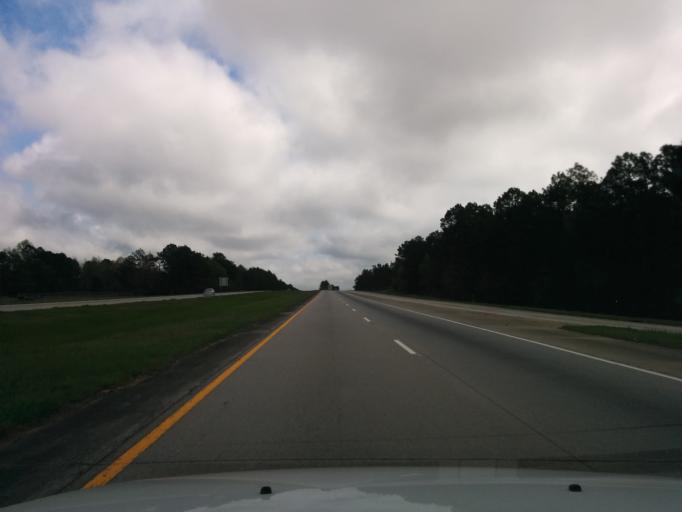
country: US
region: Georgia
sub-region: Emanuel County
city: Swainsboro
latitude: 32.4174
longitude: -82.3891
